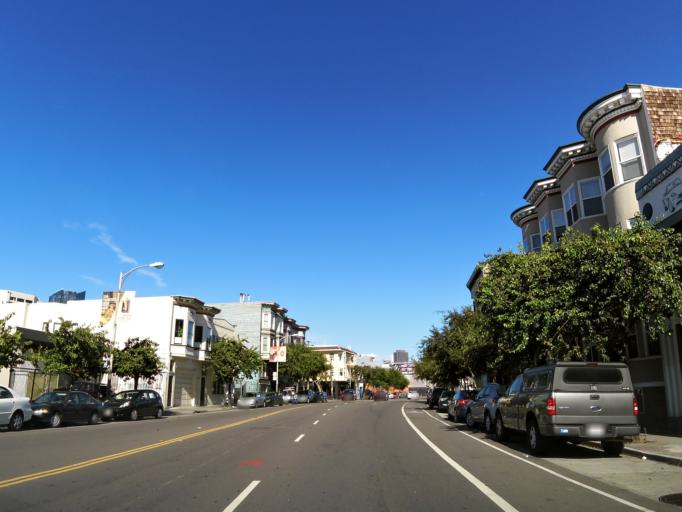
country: US
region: California
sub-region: San Francisco County
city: San Francisco
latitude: 37.7700
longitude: -122.4154
